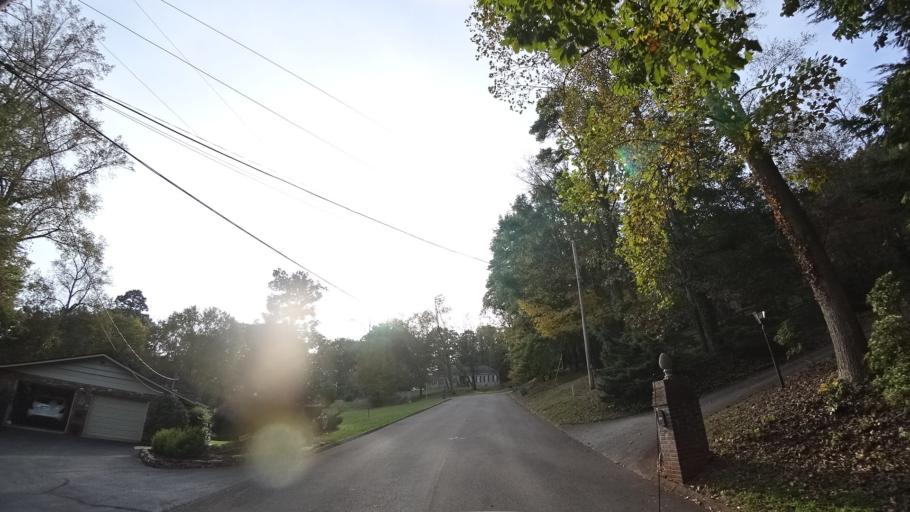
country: US
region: Tennessee
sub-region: Knox County
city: Knoxville
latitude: 35.9107
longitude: -83.9916
